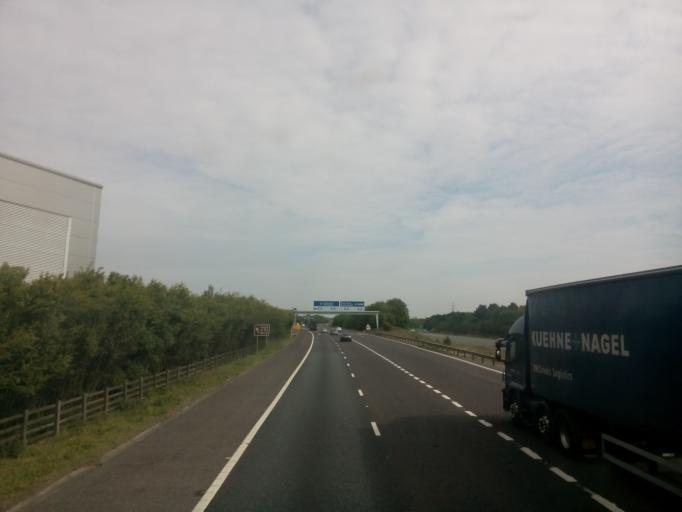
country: GB
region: England
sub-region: County Durham
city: Chester-le-Street
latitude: 54.8968
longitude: -1.5593
